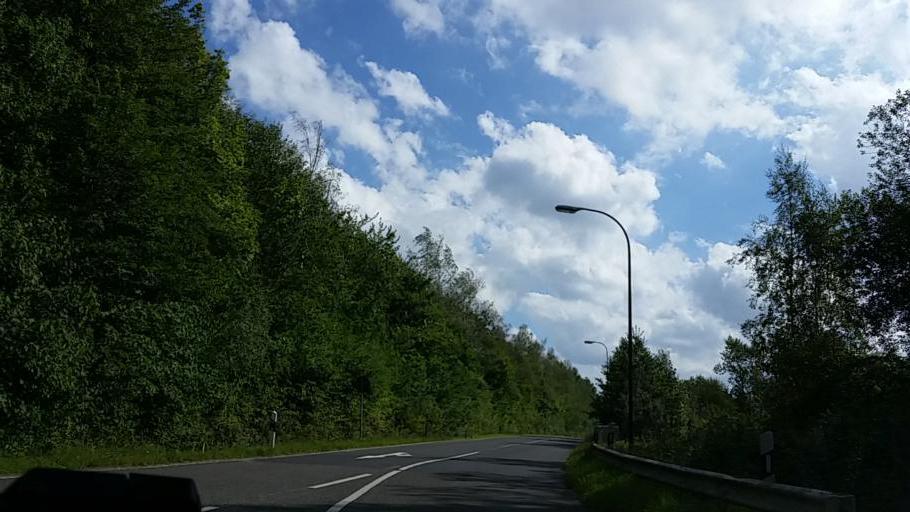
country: DE
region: North Rhine-Westphalia
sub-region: Regierungsbezirk Dusseldorf
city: Grevenbroich
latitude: 51.0453
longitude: 6.5656
